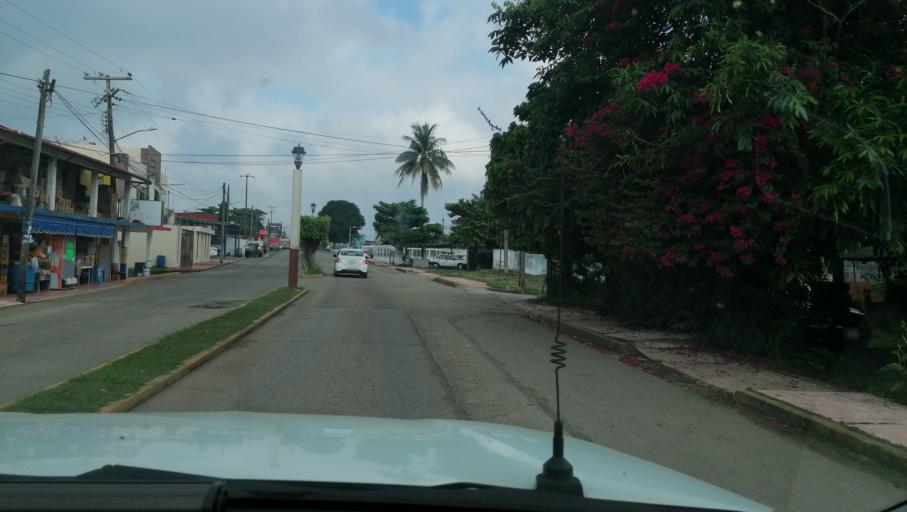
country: MX
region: Chiapas
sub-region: Juarez
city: El Triunfo 1ra. Seccion (Cardona)
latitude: 17.6035
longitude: -93.1864
